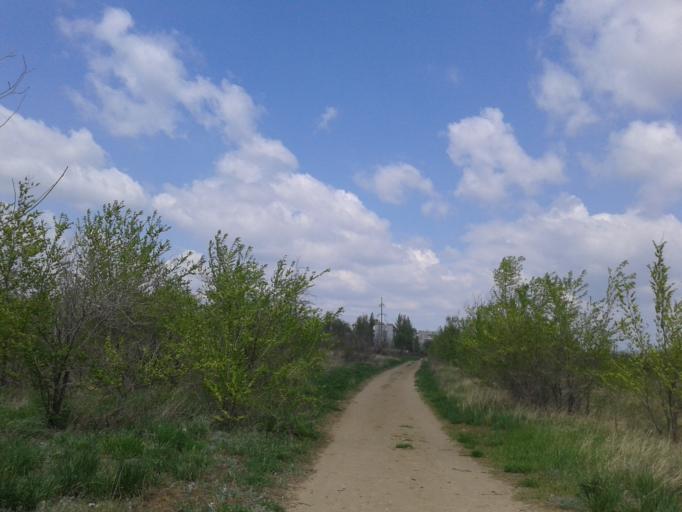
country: RU
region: Volgograd
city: Volgograd
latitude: 48.6422
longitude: 44.4359
